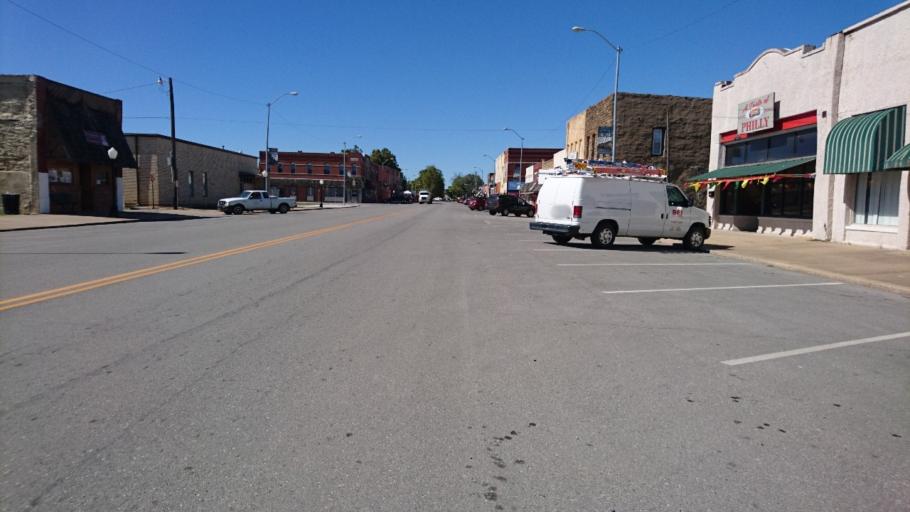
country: US
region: Oklahoma
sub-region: Rogers County
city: Chelsea
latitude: 36.5352
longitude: -95.4314
